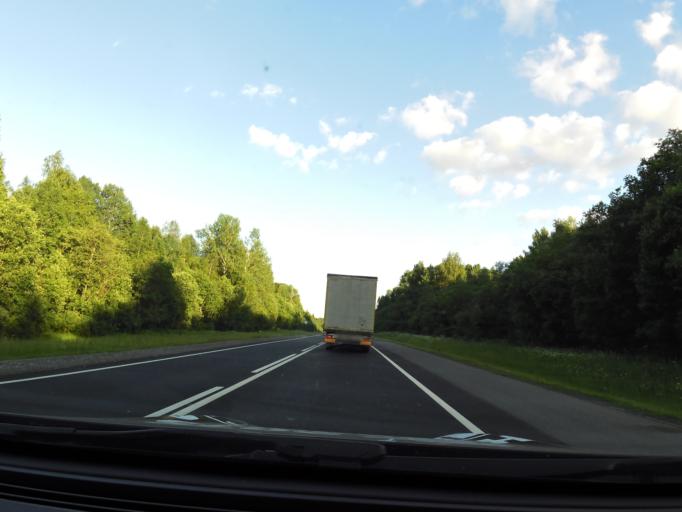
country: RU
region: Vologda
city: Gryazovets
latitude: 58.9665
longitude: 40.1572
